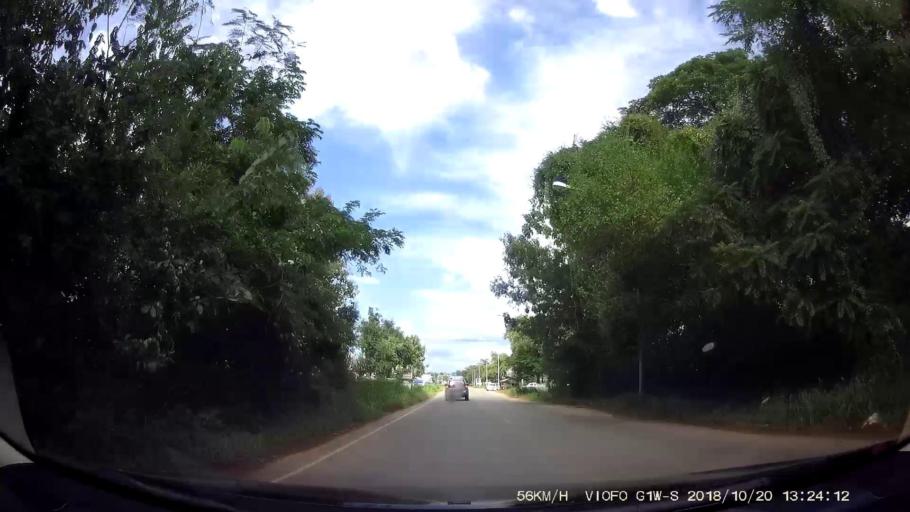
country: TH
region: Chaiyaphum
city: Khon San
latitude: 16.5913
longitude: 101.9253
